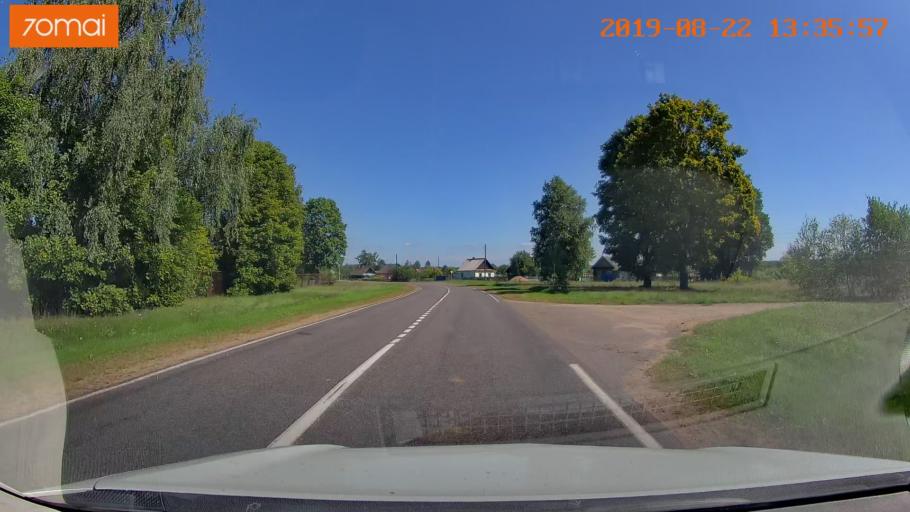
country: BY
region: Minsk
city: Staryya Darohi
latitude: 53.2129
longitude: 28.2801
